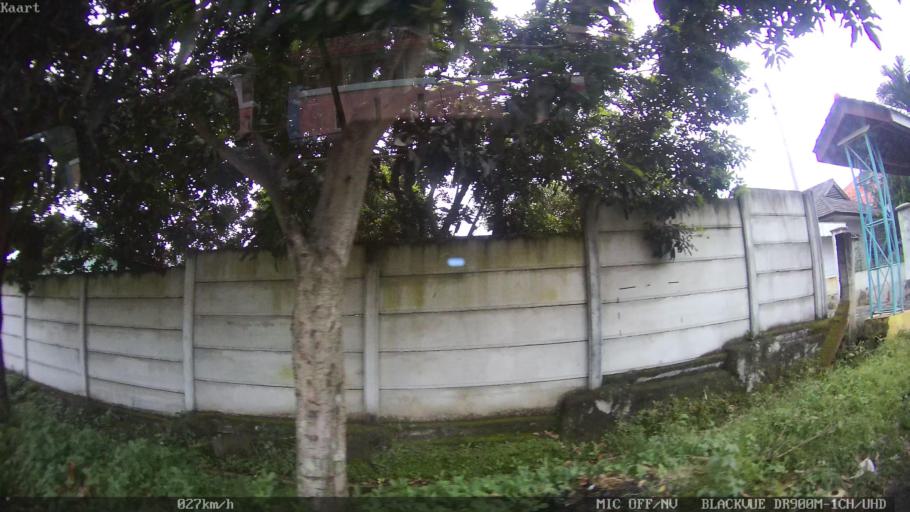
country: ID
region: Lampung
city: Kedaton
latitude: -5.3977
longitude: 105.2359
